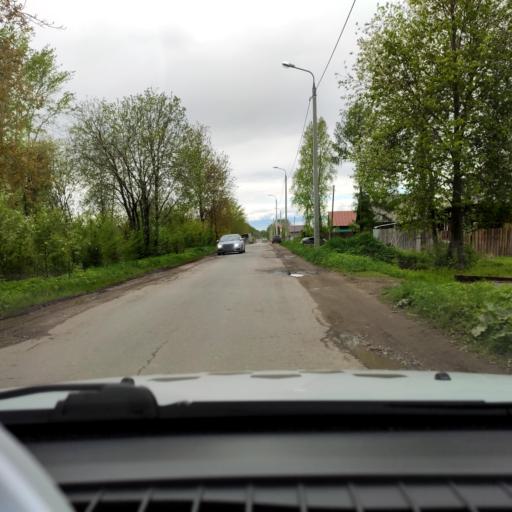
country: RU
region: Perm
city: Novyye Lyady
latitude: 58.0448
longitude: 56.6149
